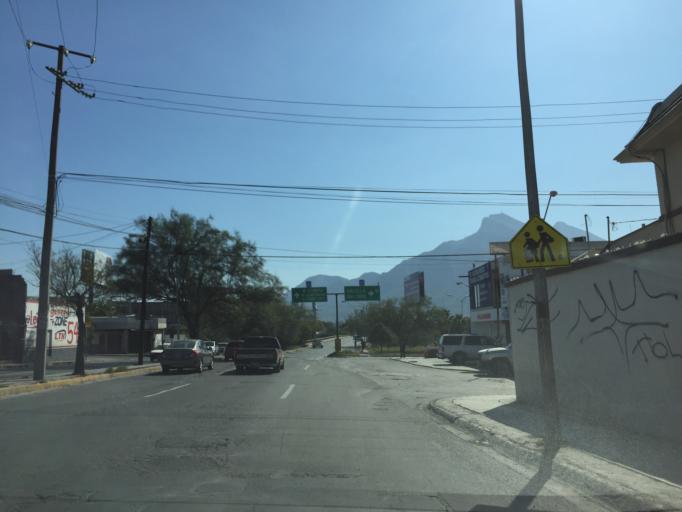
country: MX
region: Nuevo Leon
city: Guadalupe
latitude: 25.6948
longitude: -100.2303
